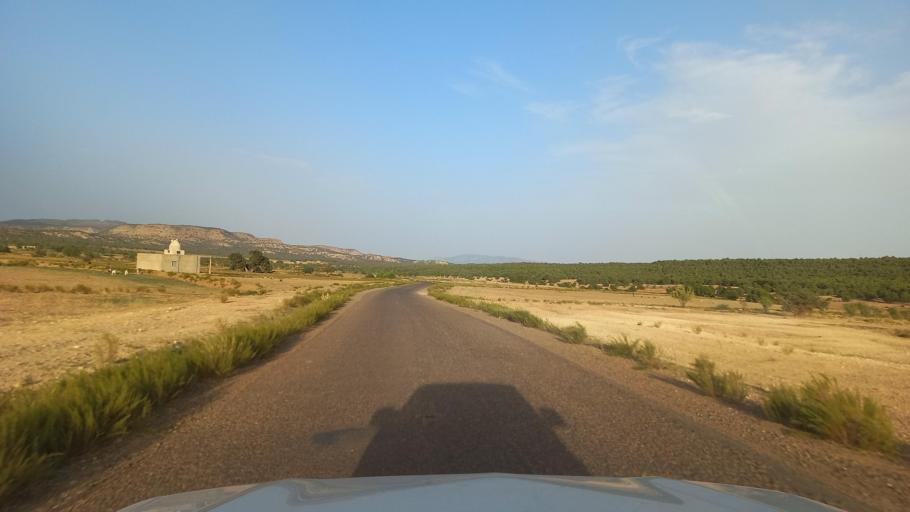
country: TN
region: Al Qasrayn
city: Sbiba
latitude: 35.4056
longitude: 8.9041
